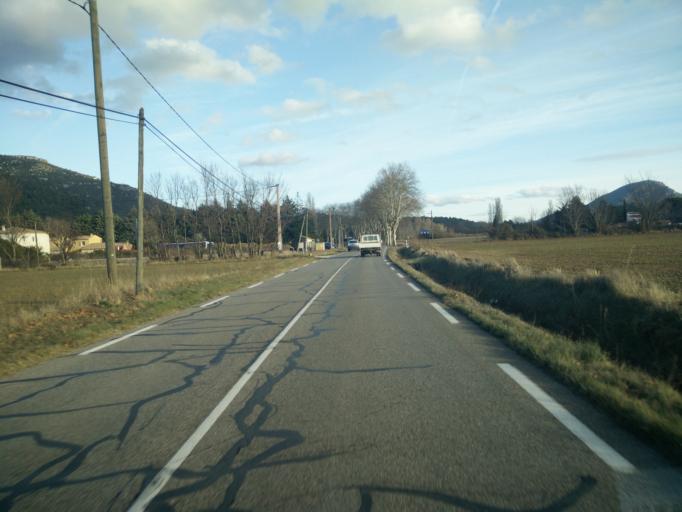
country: FR
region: Provence-Alpes-Cote d'Azur
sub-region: Departement du Var
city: Signes
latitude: 43.2875
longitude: 5.8822
